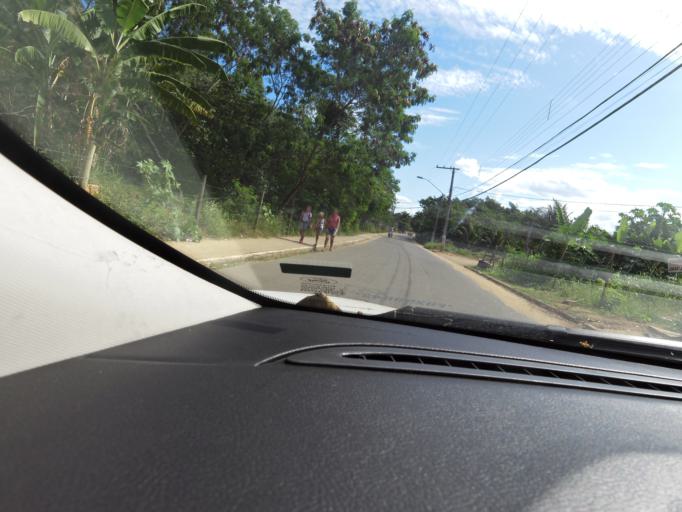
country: BR
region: Espirito Santo
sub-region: Guarapari
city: Guarapari
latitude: -20.6617
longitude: -40.5140
